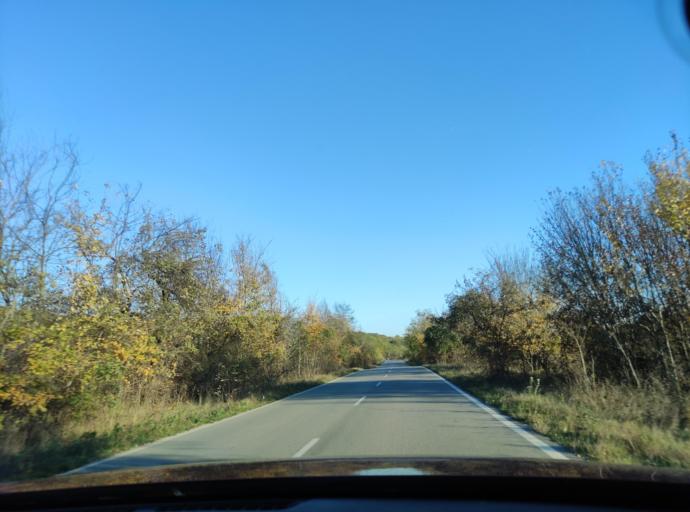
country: BG
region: Montana
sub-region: Obshtina Chiprovtsi
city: Chiprovtsi
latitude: 43.4125
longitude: 23.0422
